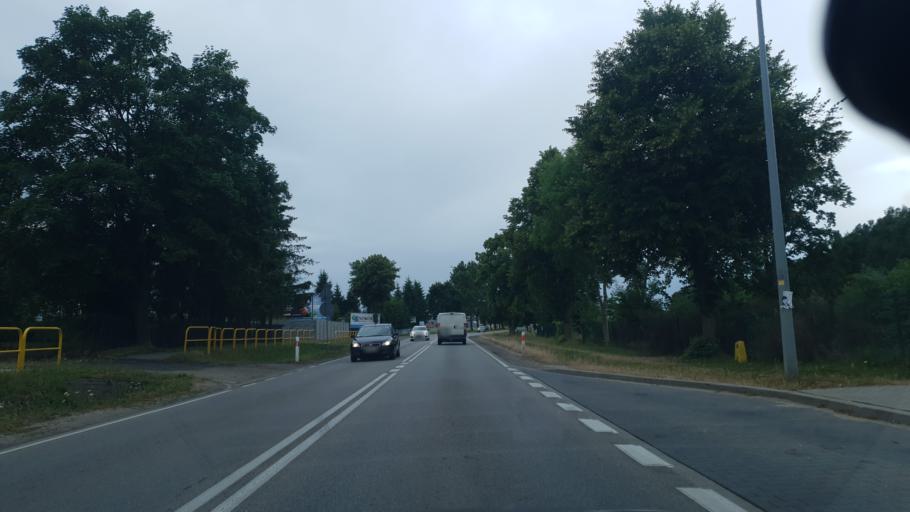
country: PL
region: Pomeranian Voivodeship
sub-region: Powiat kartuski
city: Banino
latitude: 54.4102
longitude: 18.3701
